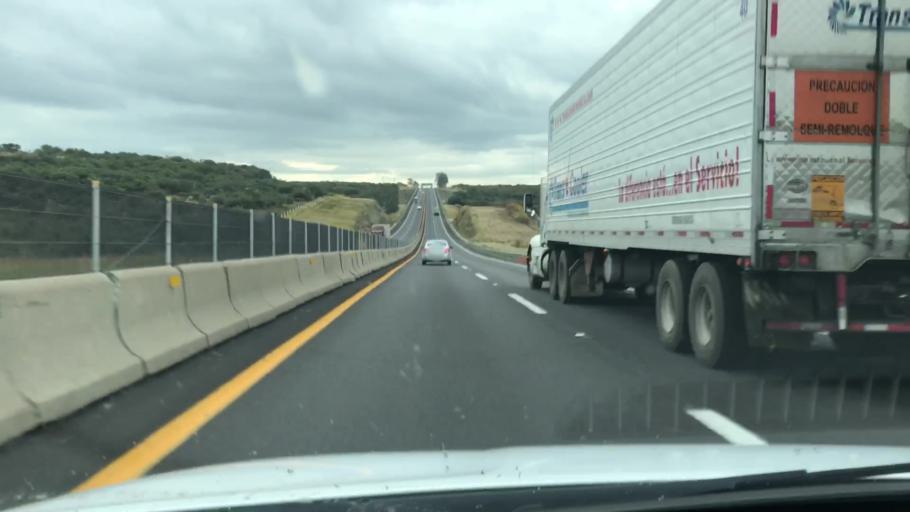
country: MX
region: Guanajuato
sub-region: Leon
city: Rizos de la Joya (Rizos del Saucillo)
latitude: 21.1274
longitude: -101.8168
